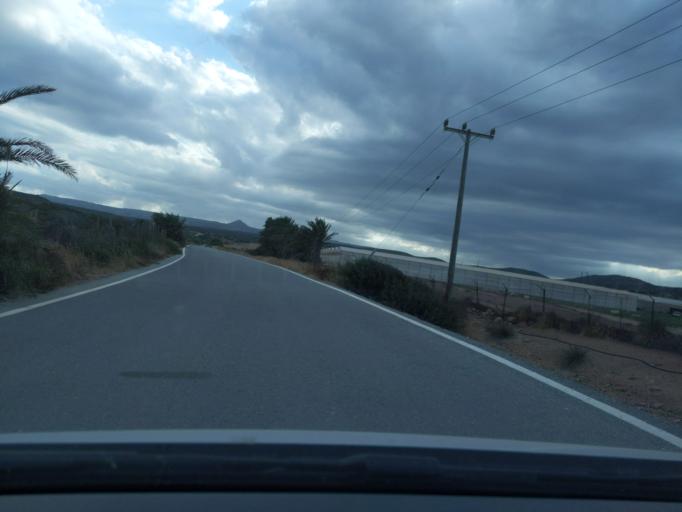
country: GR
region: Crete
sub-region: Nomos Lasithiou
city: Palekastro
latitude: 35.2614
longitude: 26.2572
